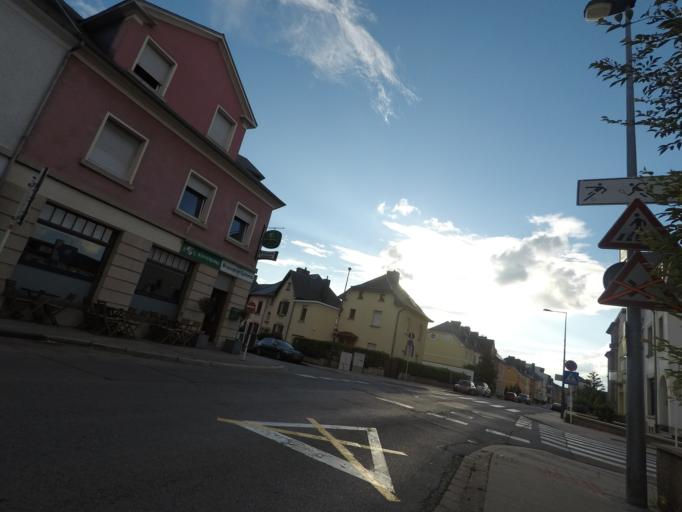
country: LU
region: Luxembourg
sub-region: Canton de Luxembourg
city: Luxembourg
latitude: 49.5900
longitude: 6.1277
